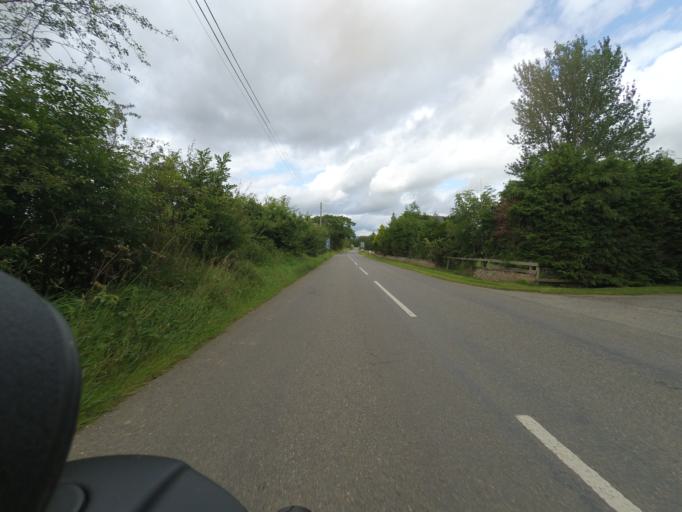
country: GB
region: Scotland
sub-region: Aberdeenshire
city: Laurencekirk
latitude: 56.8415
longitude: -2.5678
